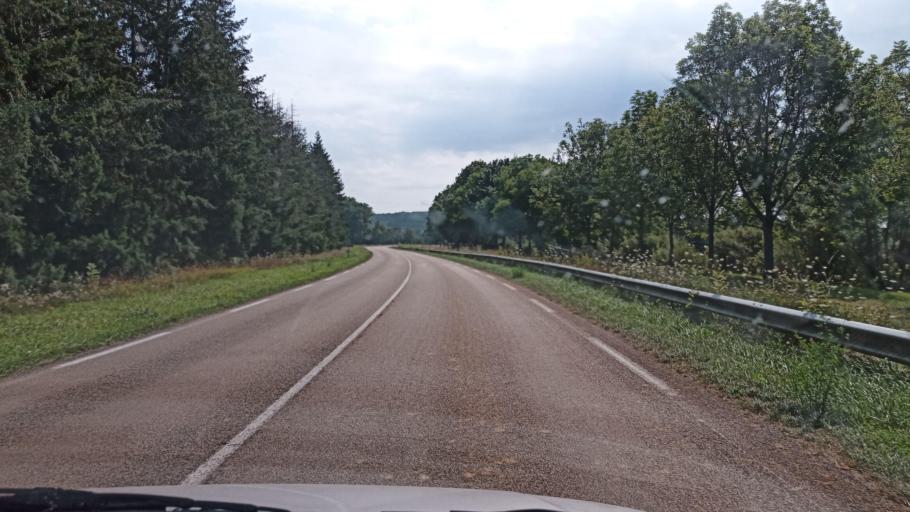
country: FR
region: Bourgogne
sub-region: Departement de l'Yonne
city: Villeneuve-sur-Yonne
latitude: 48.0964
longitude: 3.2801
